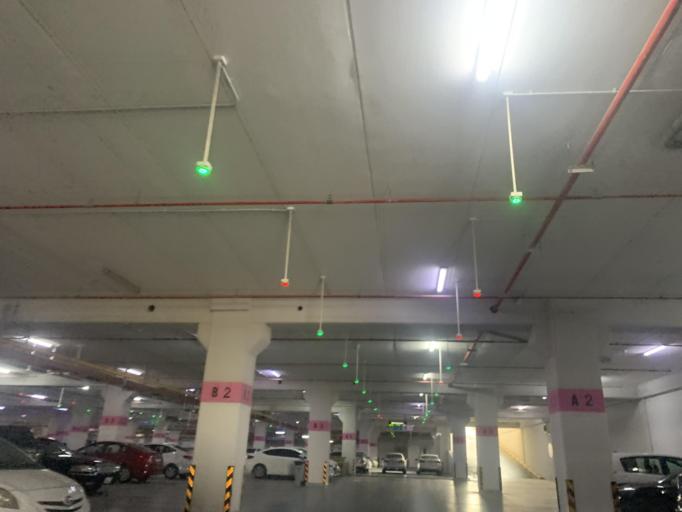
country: BH
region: Northern
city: Madinat `Isa
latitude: 26.1765
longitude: 50.4838
